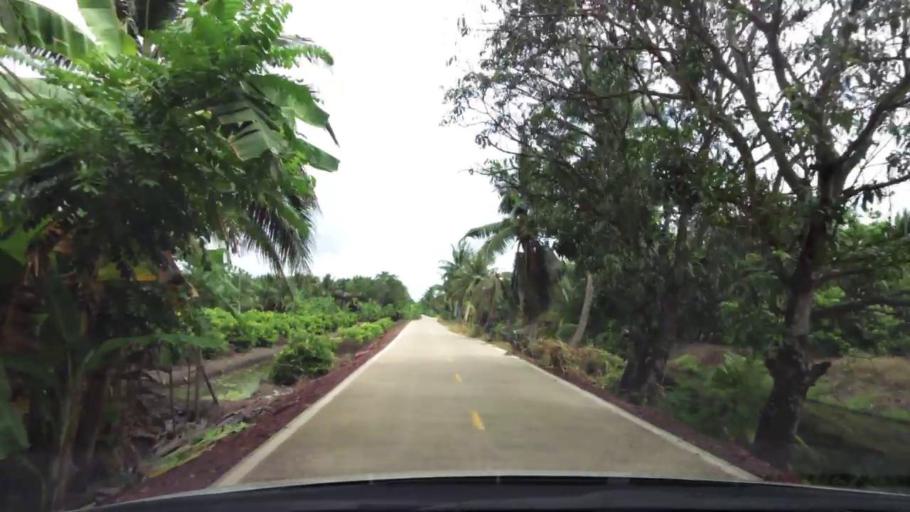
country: TH
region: Ratchaburi
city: Damnoen Saduak
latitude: 13.5548
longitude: 99.9811
